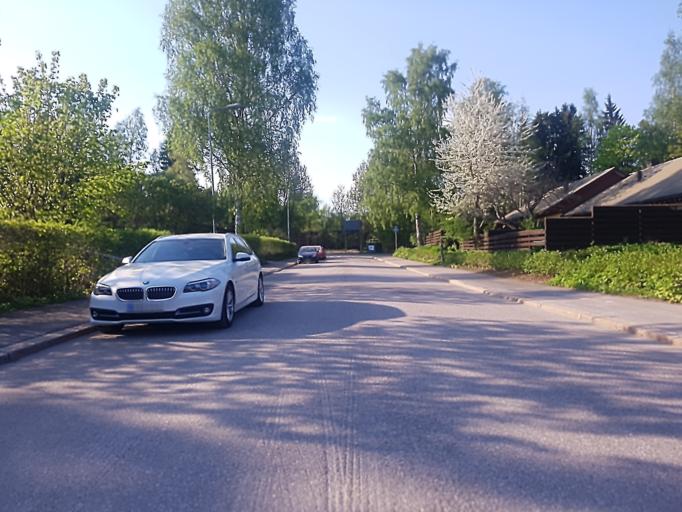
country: FI
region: Uusimaa
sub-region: Helsinki
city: Helsinki
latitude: 60.2381
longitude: 24.9170
